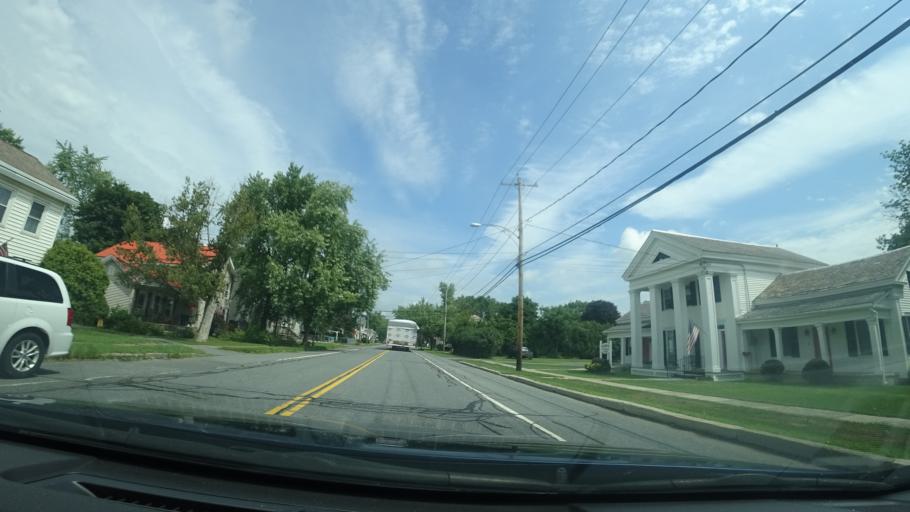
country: US
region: New York
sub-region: Warren County
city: Queensbury
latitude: 43.4110
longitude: -73.4889
